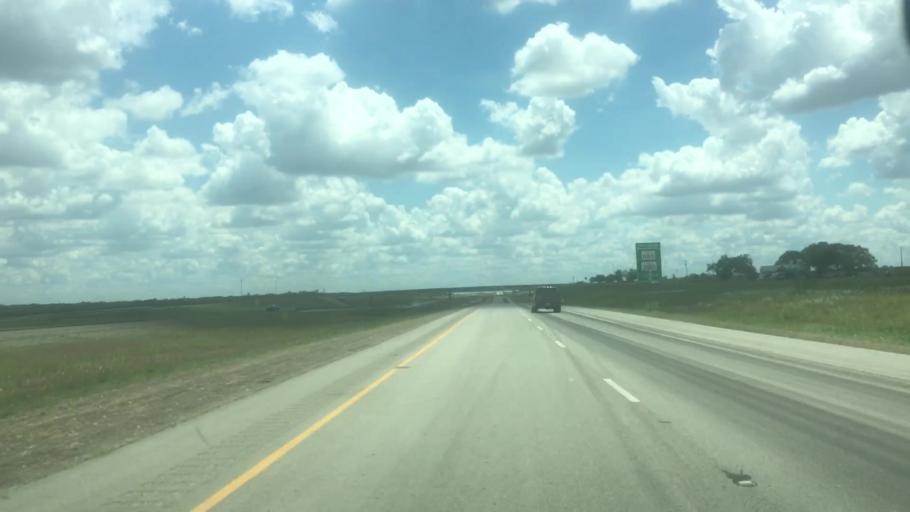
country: US
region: Texas
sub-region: Caldwell County
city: Lockhart
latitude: 29.9717
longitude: -97.6791
